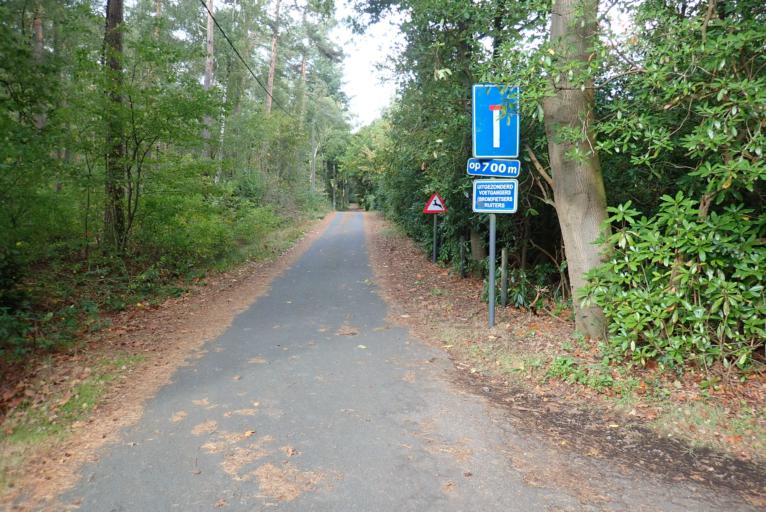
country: BE
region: Flanders
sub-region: Provincie Antwerpen
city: Essen
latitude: 51.4363
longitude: 4.4578
